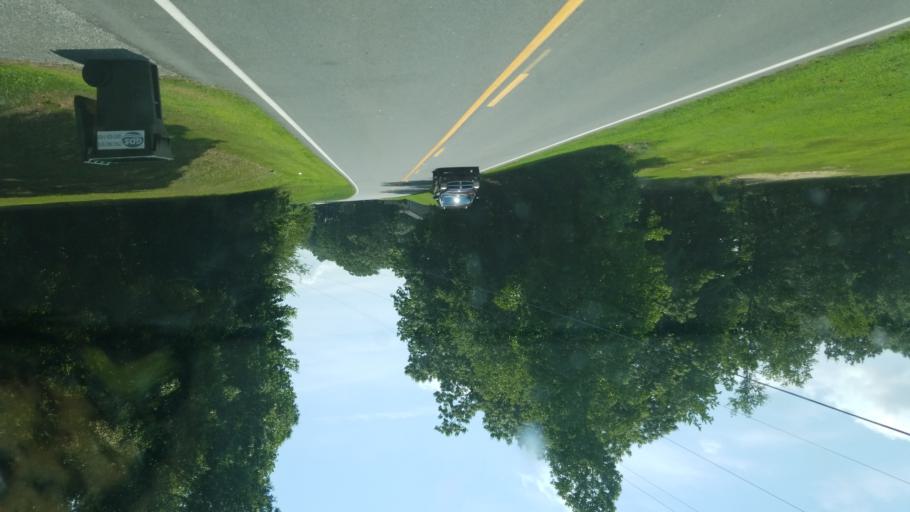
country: US
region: North Carolina
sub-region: Gaston County
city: Cherryville
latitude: 35.3602
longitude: -81.3605
